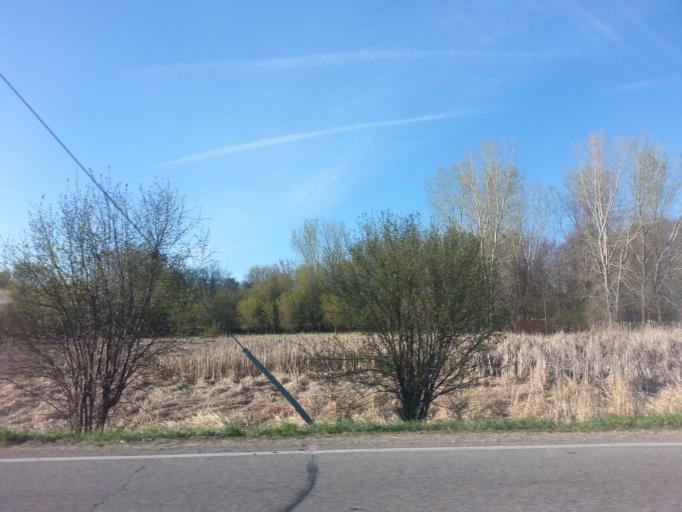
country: US
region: Minnesota
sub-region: Rice County
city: Northfield
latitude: 44.5437
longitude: -93.1577
